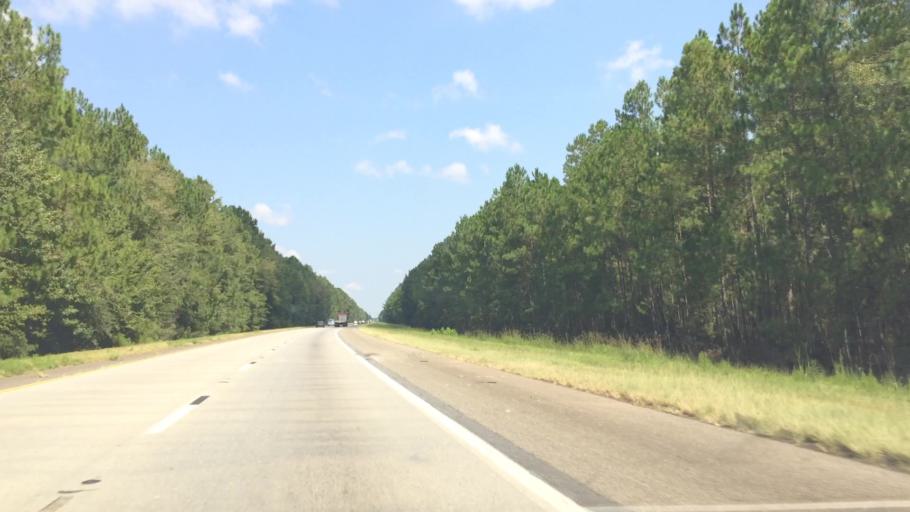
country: US
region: South Carolina
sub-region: Colleton County
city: Walterboro
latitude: 33.0485
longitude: -80.6682
